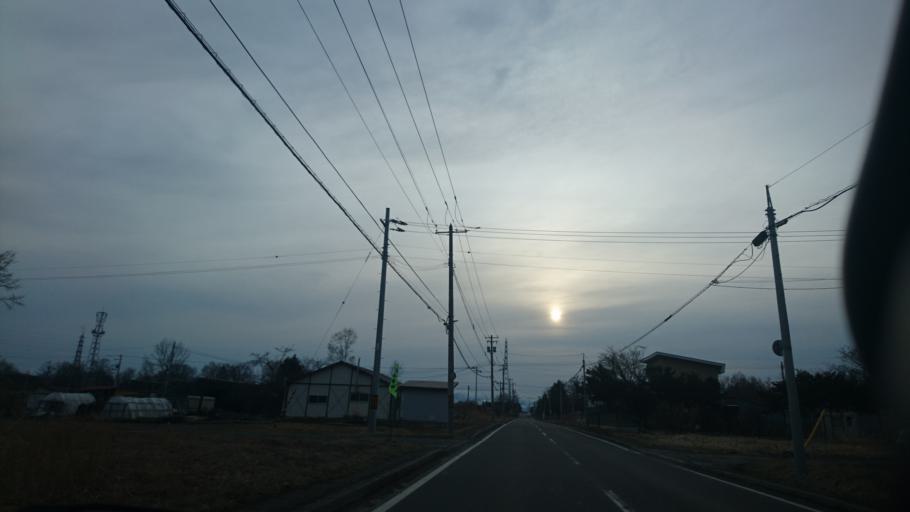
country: JP
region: Hokkaido
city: Otofuke
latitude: 42.9771
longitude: 143.2020
